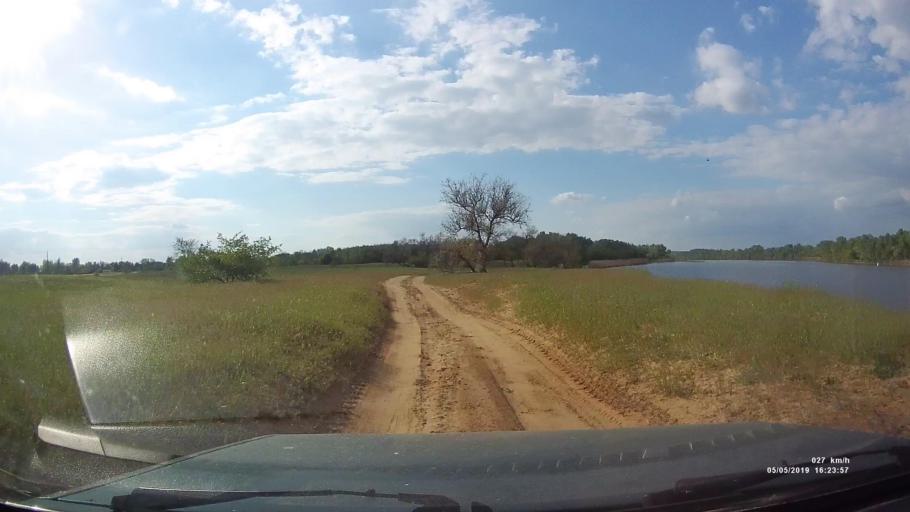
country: RU
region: Rostov
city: Konstantinovsk
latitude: 47.7577
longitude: 41.0283
